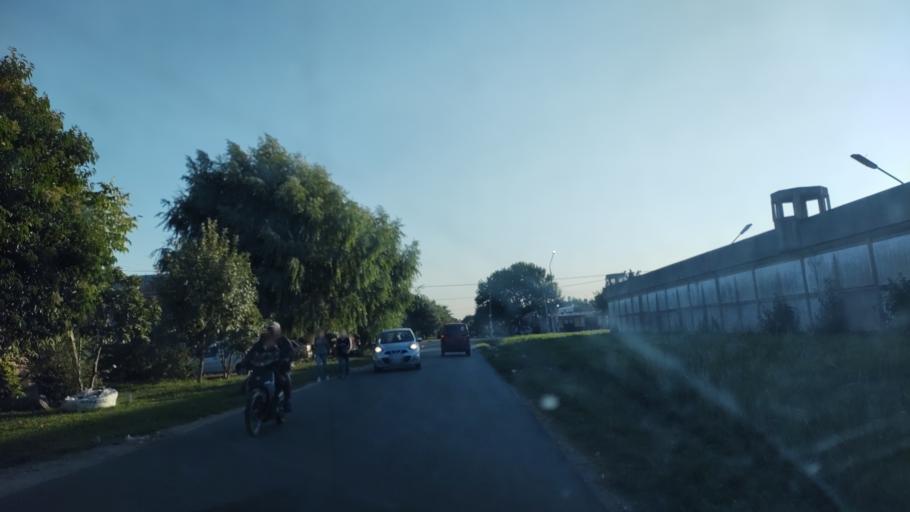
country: AR
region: Buenos Aires
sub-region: Partido de La Plata
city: La Plata
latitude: -34.9702
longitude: -57.9709
